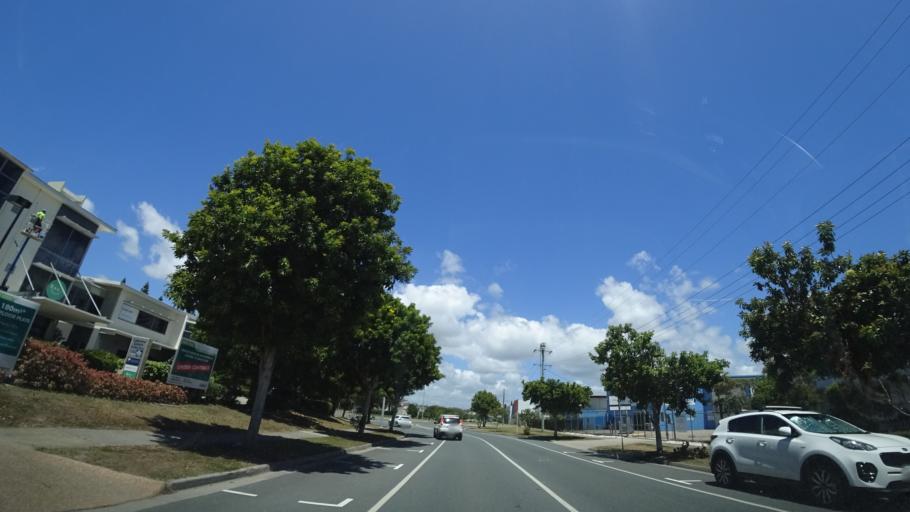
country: AU
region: Queensland
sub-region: Sunshine Coast
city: Mooloolaba
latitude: -26.7308
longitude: 153.1235
